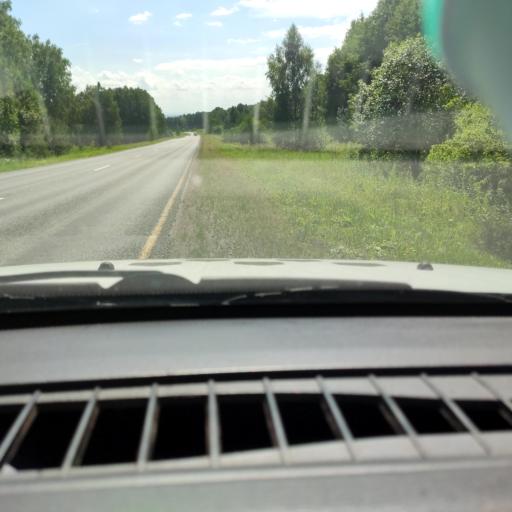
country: RU
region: Bashkortostan
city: Mesyagutovo
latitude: 55.4957
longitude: 58.3236
